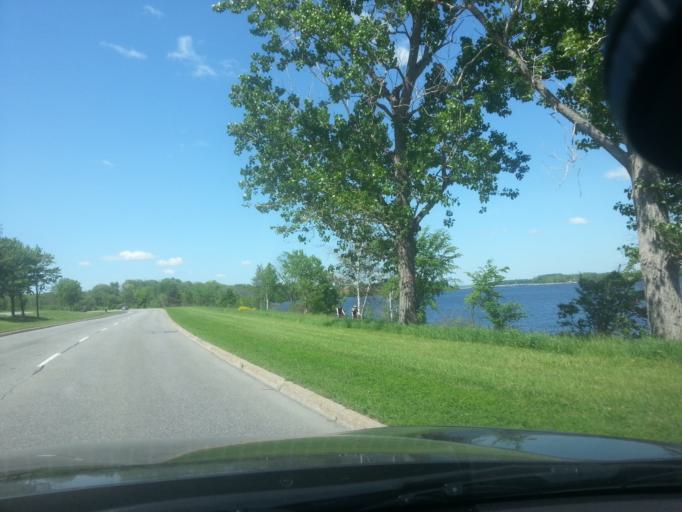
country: CA
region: Ontario
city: Bells Corners
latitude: 45.3755
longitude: -75.7820
